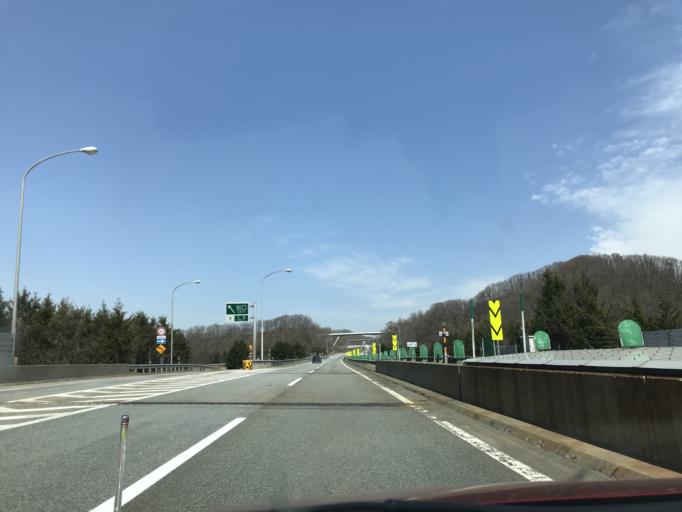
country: JP
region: Hokkaido
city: Iwamizawa
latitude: 43.2419
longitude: 141.8303
